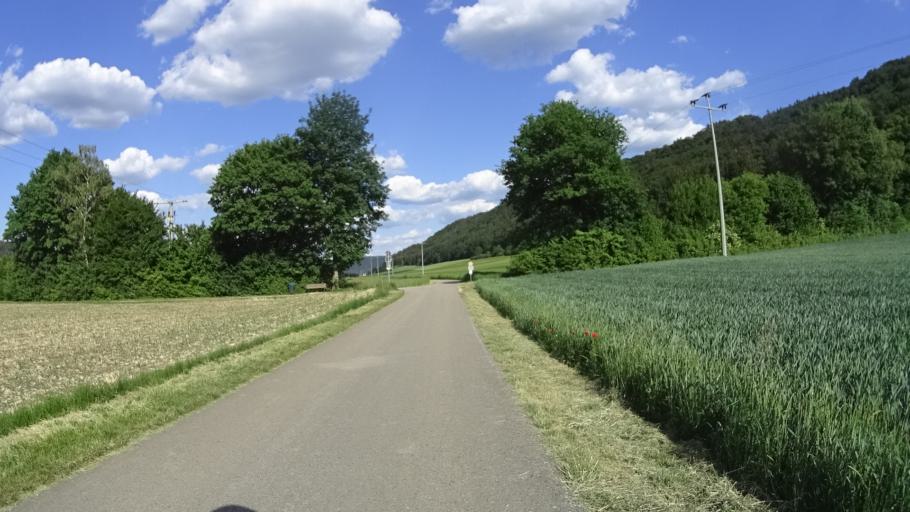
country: DE
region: Bavaria
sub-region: Upper Palatinate
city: Dietfurt
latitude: 49.0185
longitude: 11.4978
